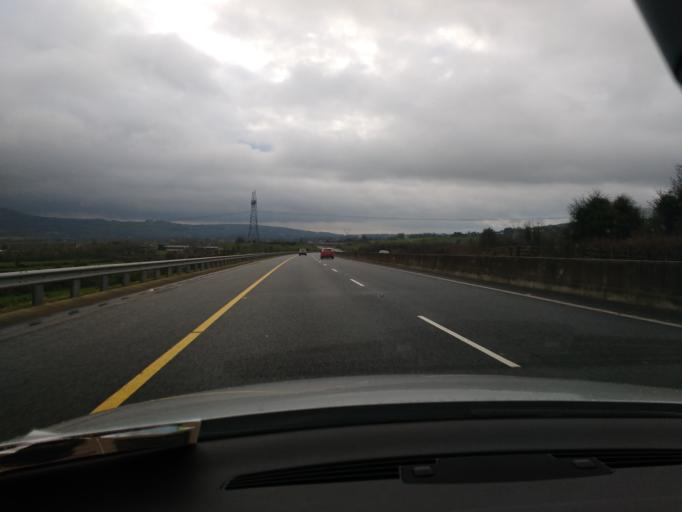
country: IE
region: Munster
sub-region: North Tipperary
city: Nenagh
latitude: 52.8314
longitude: -8.2919
